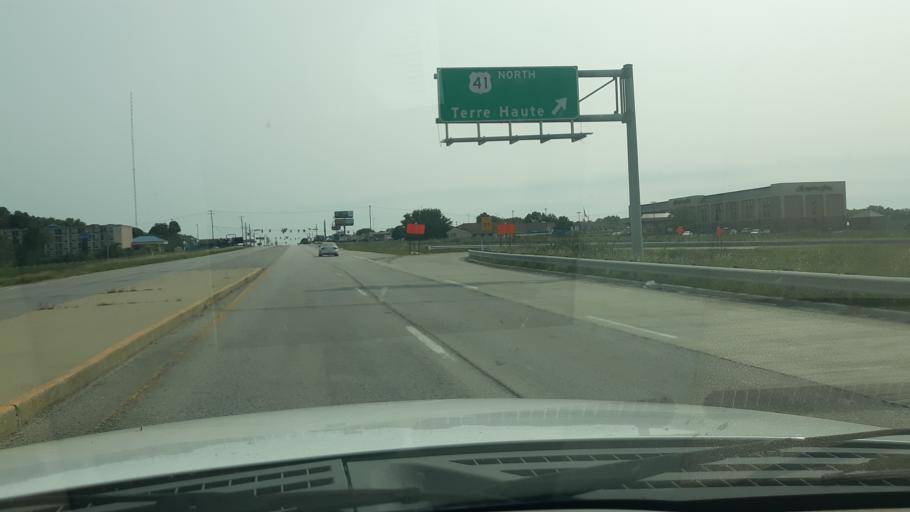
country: US
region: Indiana
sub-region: Gibson County
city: Princeton
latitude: 38.3555
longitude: -87.5983
